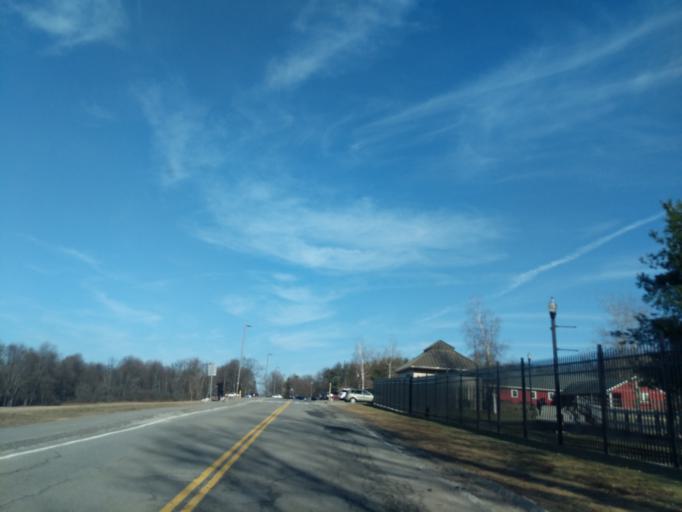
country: US
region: Massachusetts
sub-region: Worcester County
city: Worcester
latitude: 42.2818
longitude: -71.7814
